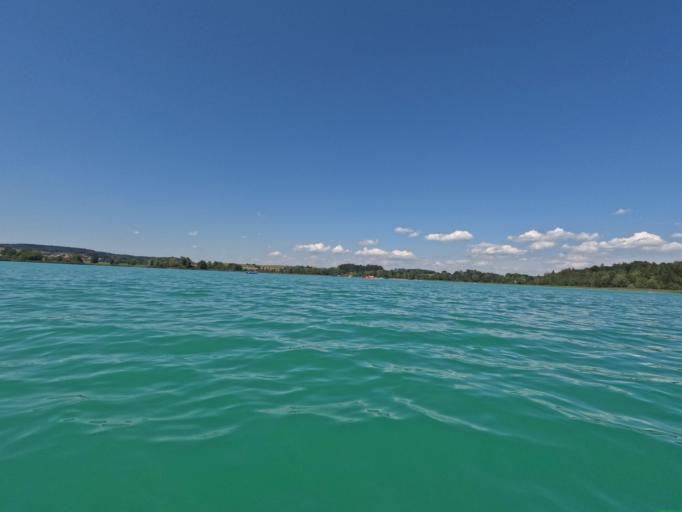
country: DE
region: Bavaria
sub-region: Upper Bavaria
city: Taching am See
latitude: 47.9803
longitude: 12.7450
